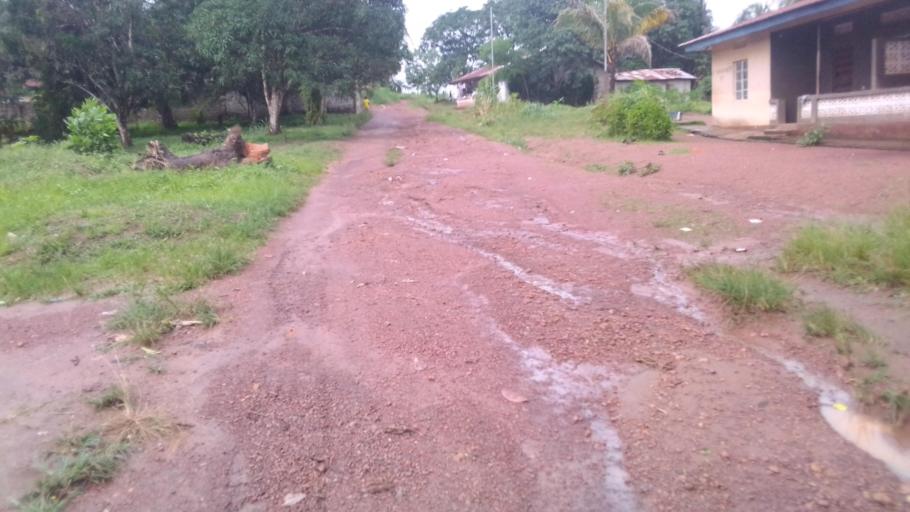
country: SL
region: Eastern Province
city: Kenema
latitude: 7.8517
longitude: -11.1960
